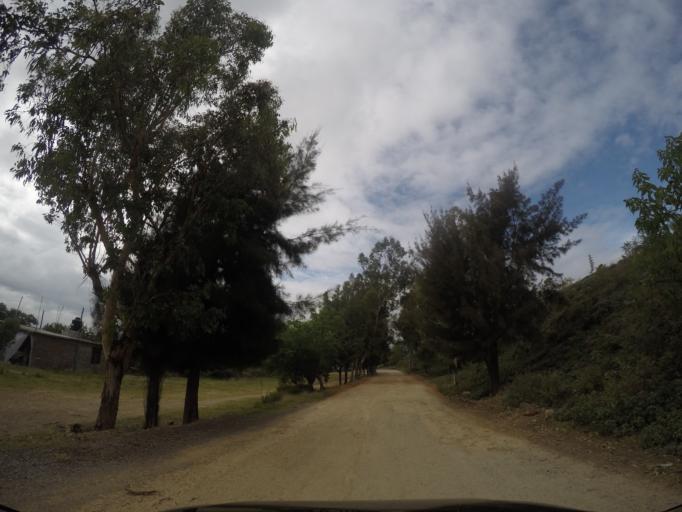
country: MX
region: Oaxaca
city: San Lorenzo Albarradas
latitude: 16.8703
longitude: -96.2771
